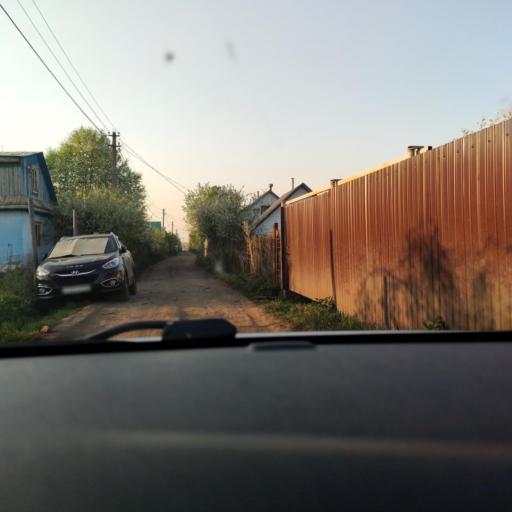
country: RU
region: Bashkortostan
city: Avdon
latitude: 54.7168
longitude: 55.7910
